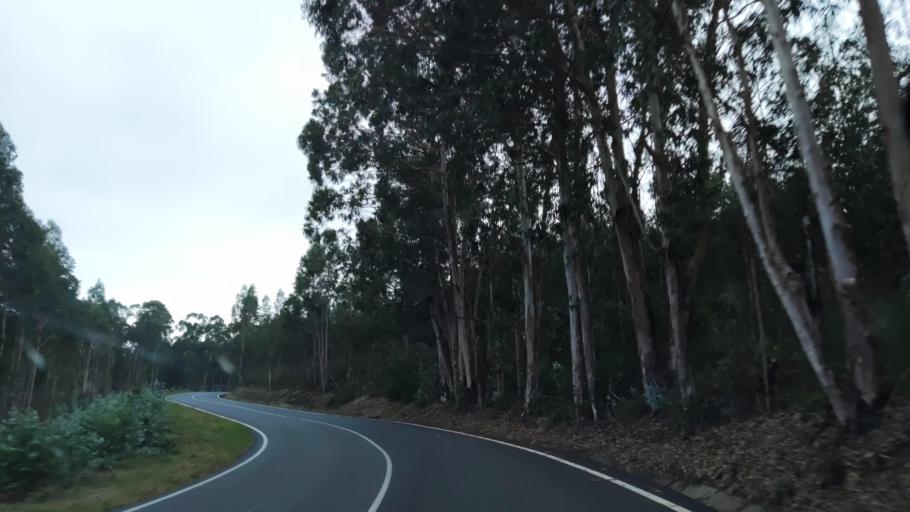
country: ES
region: Galicia
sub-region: Provincia de Pontevedra
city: Catoira
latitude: 42.6572
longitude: -8.7522
